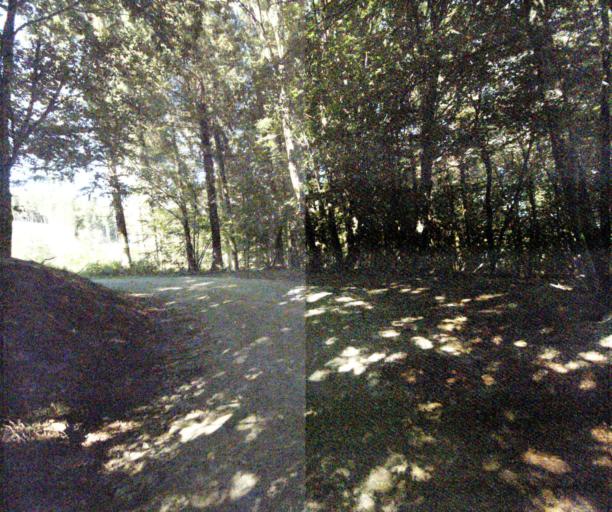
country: FR
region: Midi-Pyrenees
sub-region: Departement du Tarn
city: Dourgne
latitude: 43.4367
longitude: 2.1379
